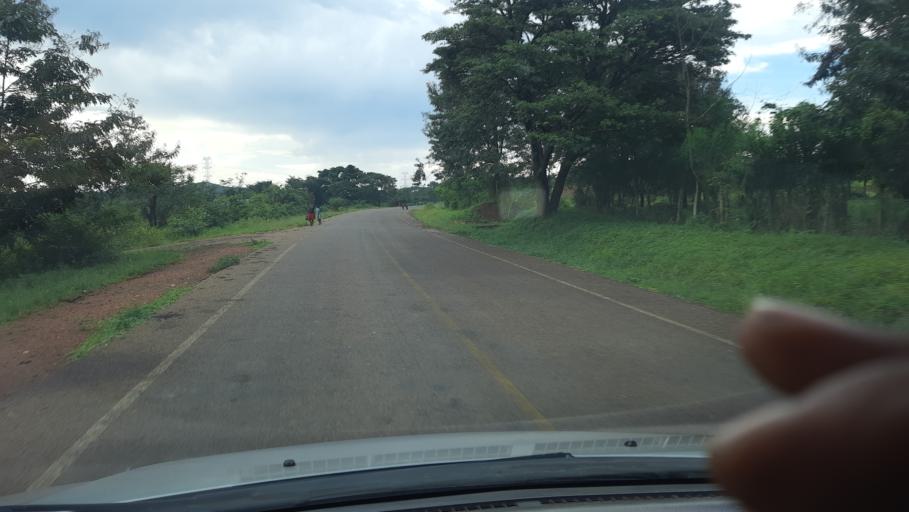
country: UG
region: Central Region
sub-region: Nakasongola District
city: Nakasongola
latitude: 1.3150
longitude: 32.4405
